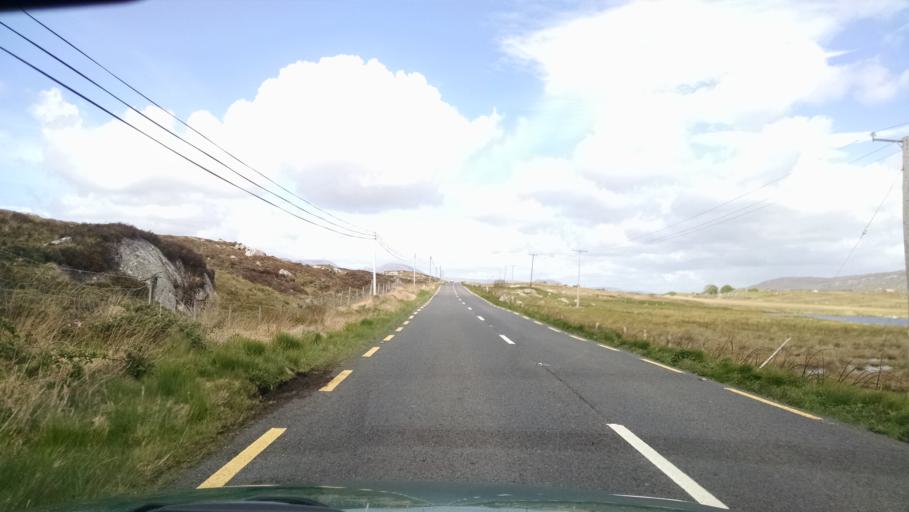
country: IE
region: Connaught
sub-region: County Galway
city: Oughterard
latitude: 53.3526
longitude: -9.5418
